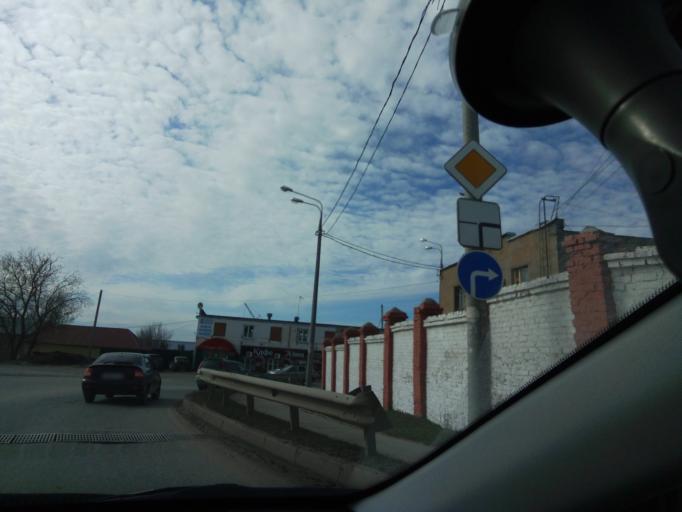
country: RU
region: Chuvashia
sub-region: Cheboksarskiy Rayon
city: Cheboksary
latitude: 56.1027
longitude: 47.2507
